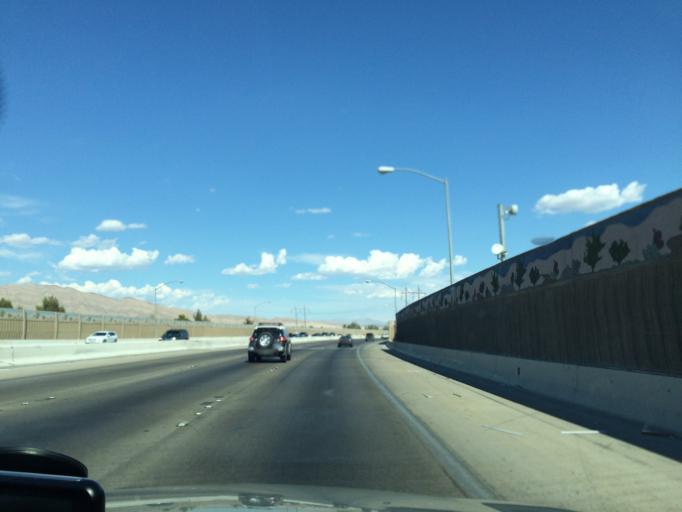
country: US
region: Nevada
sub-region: Clark County
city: North Las Vegas
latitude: 36.1669
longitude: -115.0988
